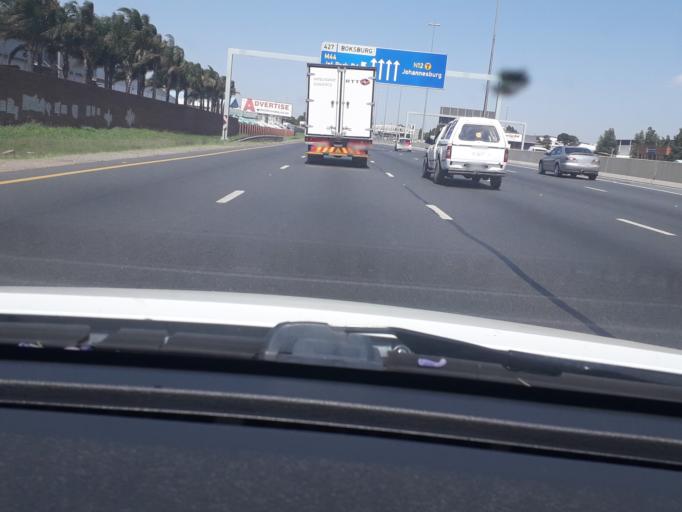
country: ZA
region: Gauteng
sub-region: Ekurhuleni Metropolitan Municipality
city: Boksburg
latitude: -26.1764
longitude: 28.2242
